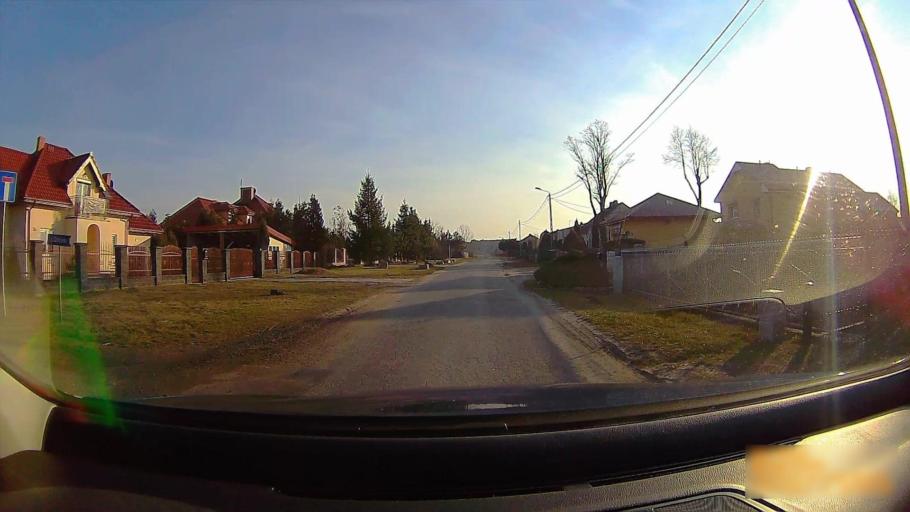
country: PL
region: Greater Poland Voivodeship
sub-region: Konin
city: Konin
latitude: 52.1830
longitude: 18.3012
